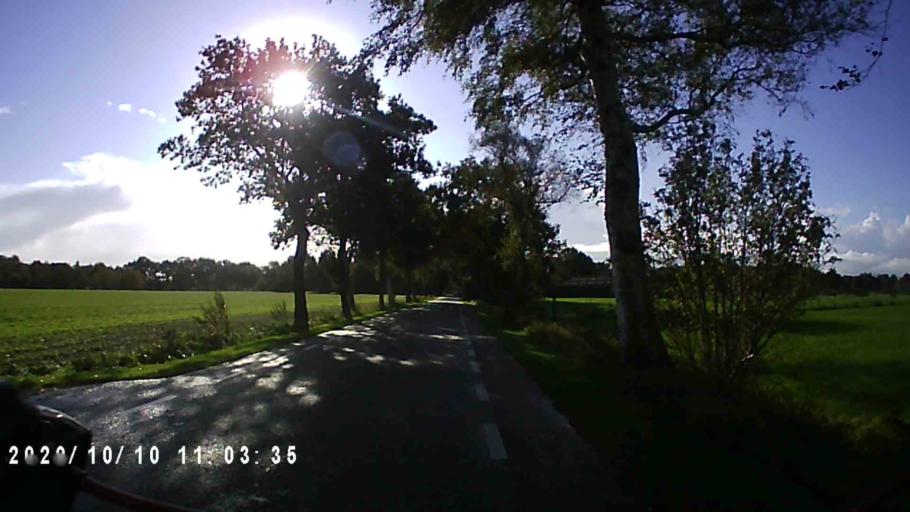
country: NL
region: Friesland
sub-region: Gemeente Achtkarspelen
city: Surhuisterveen
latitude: 53.1340
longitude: 6.2231
